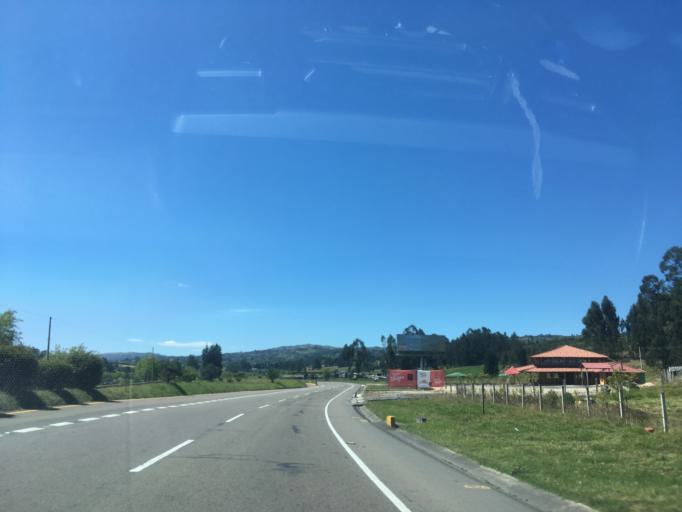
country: CO
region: Boyaca
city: Tuta
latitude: 5.7122
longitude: -73.2371
